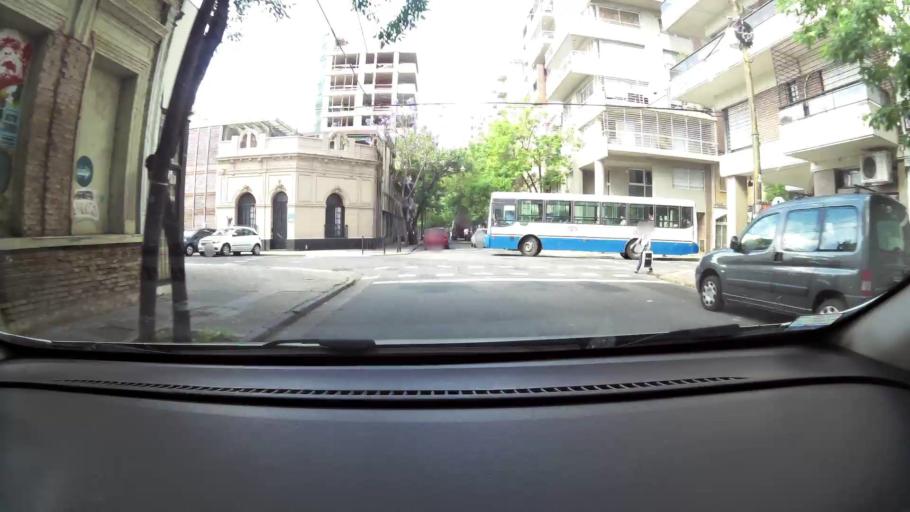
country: AR
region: Santa Fe
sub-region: Departamento de Rosario
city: Rosario
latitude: -32.9559
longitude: -60.6274
